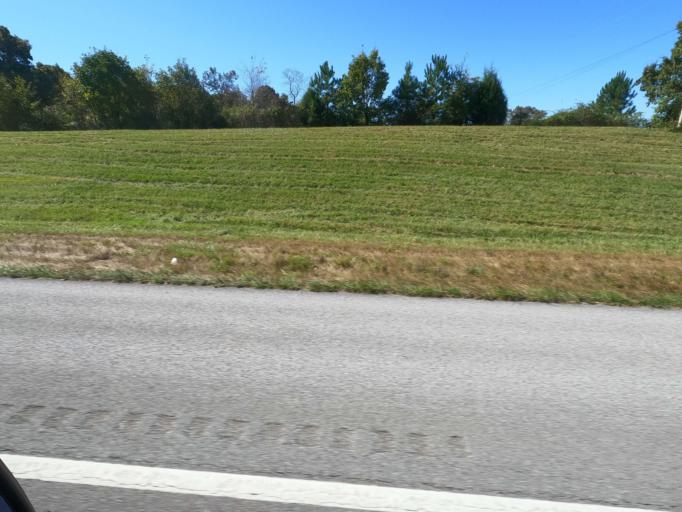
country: US
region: Tennessee
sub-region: Lawrence County
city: Lawrenceburg
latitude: 35.3874
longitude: -87.2759
